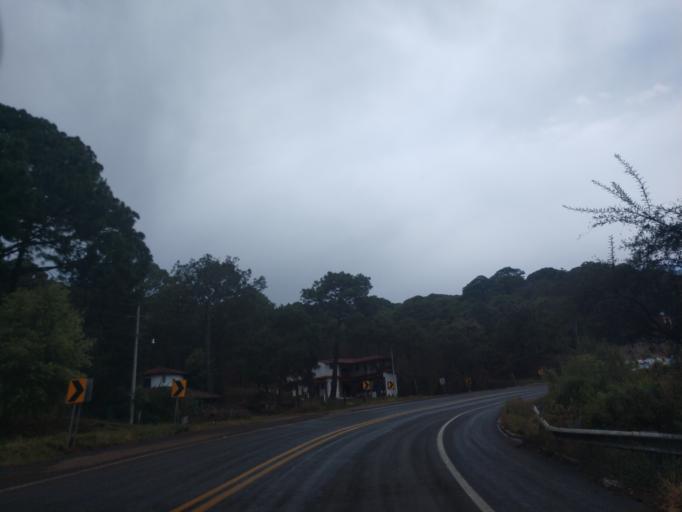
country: MX
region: Jalisco
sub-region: Mazamitla
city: Mazamitla
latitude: 19.9420
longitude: -103.0630
